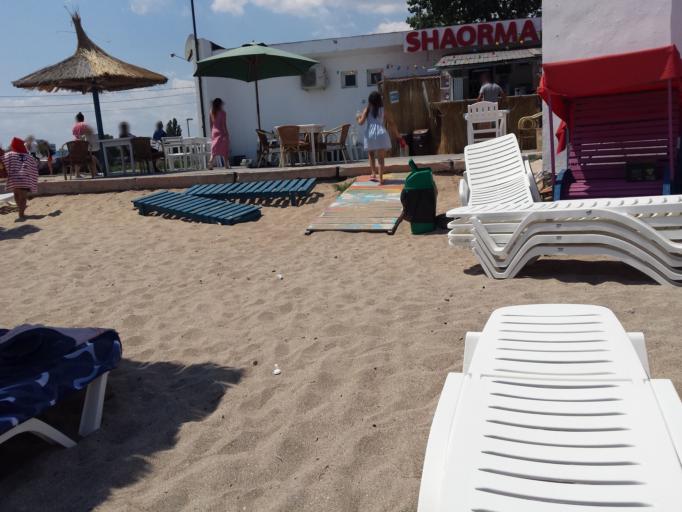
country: RO
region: Constanta
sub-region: Comuna Douazeci si Trei August
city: Douazeci si Trei August
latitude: 43.8625
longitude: 28.6060
